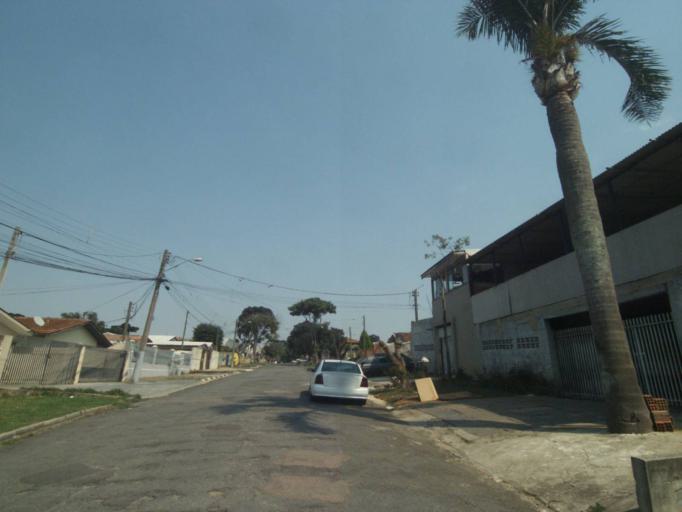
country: BR
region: Parana
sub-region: Sao Jose Dos Pinhais
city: Sao Jose dos Pinhais
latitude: -25.5237
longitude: -49.2498
